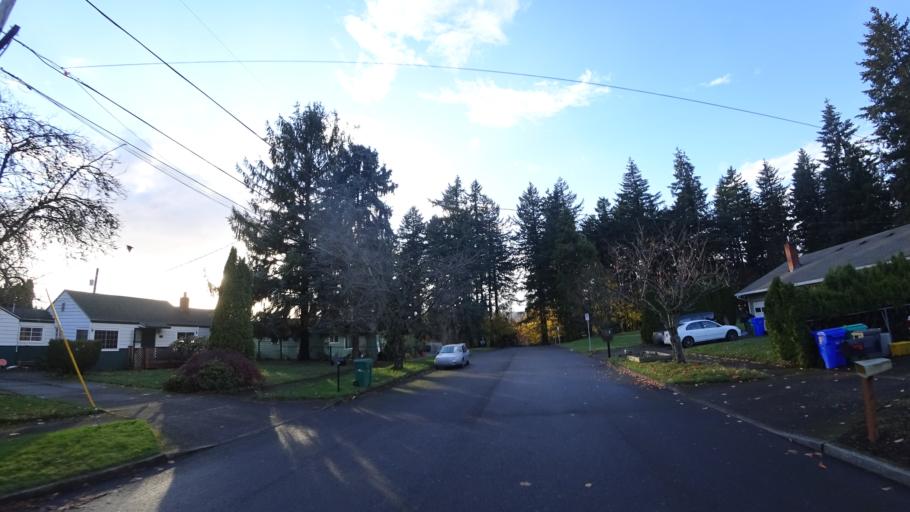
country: US
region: Oregon
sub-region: Multnomah County
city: Lents
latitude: 45.5147
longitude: -122.5500
